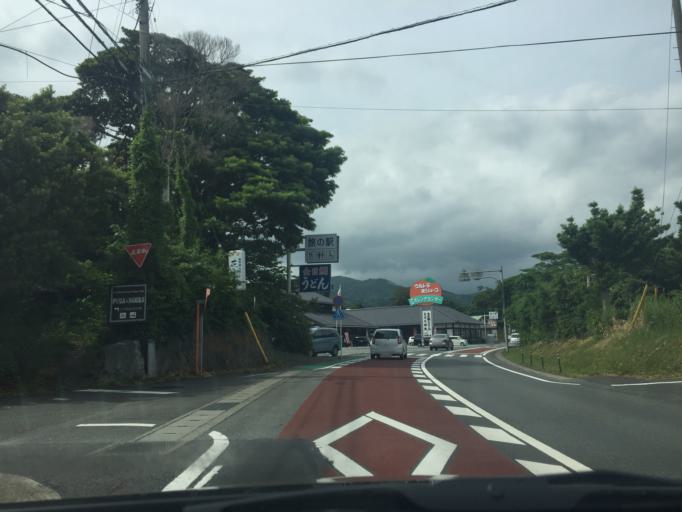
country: JP
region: Shizuoka
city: Shimoda
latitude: 34.7584
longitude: 139.0195
